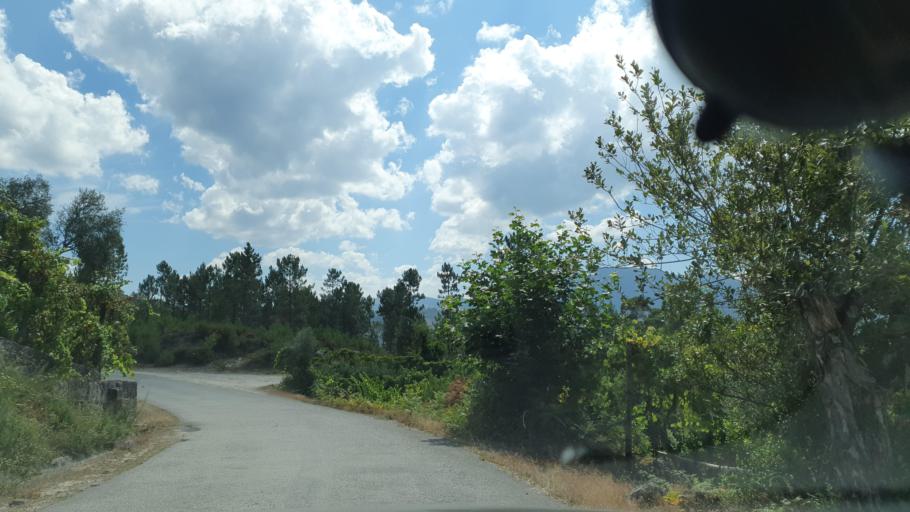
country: PT
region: Braga
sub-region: Vieira do Minho
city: Vieira do Minho
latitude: 41.7027
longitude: -8.0735
